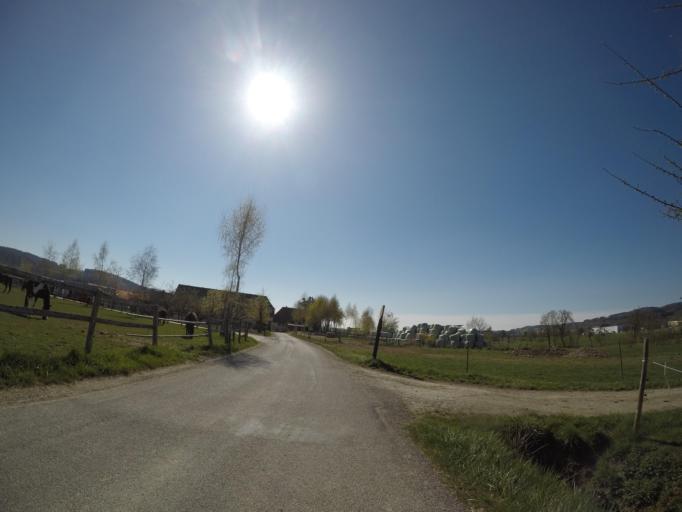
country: DE
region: Baden-Wuerttemberg
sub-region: Tuebingen Region
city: Wilhelmsdorf
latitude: 47.8581
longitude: 9.4334
